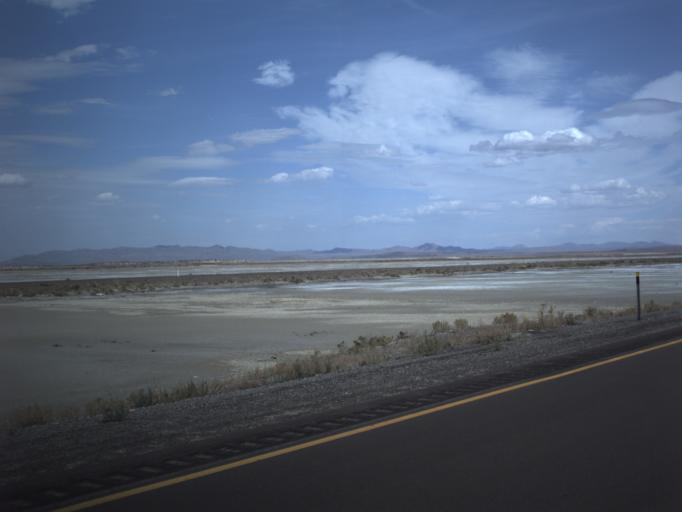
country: US
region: Utah
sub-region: Tooele County
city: Wendover
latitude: 40.7273
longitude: -113.3120
